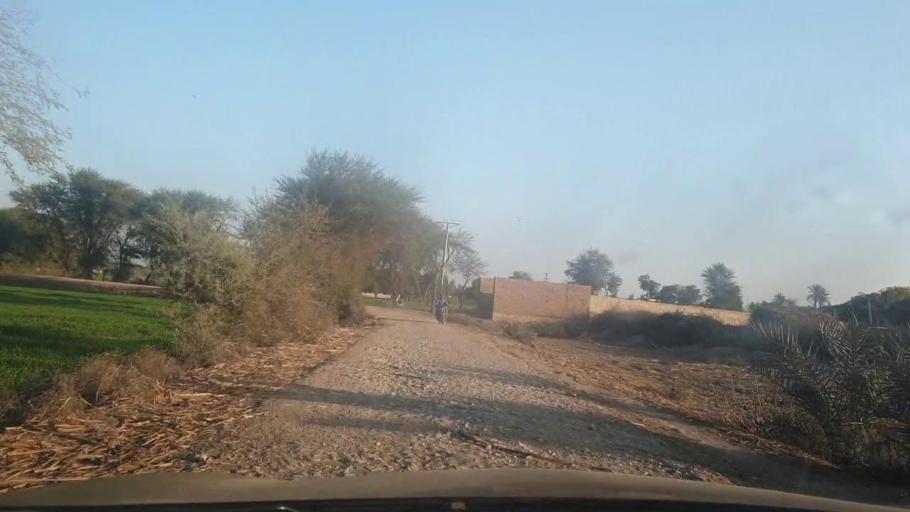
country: PK
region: Sindh
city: Mirpur Mathelo
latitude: 28.1694
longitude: 69.5787
